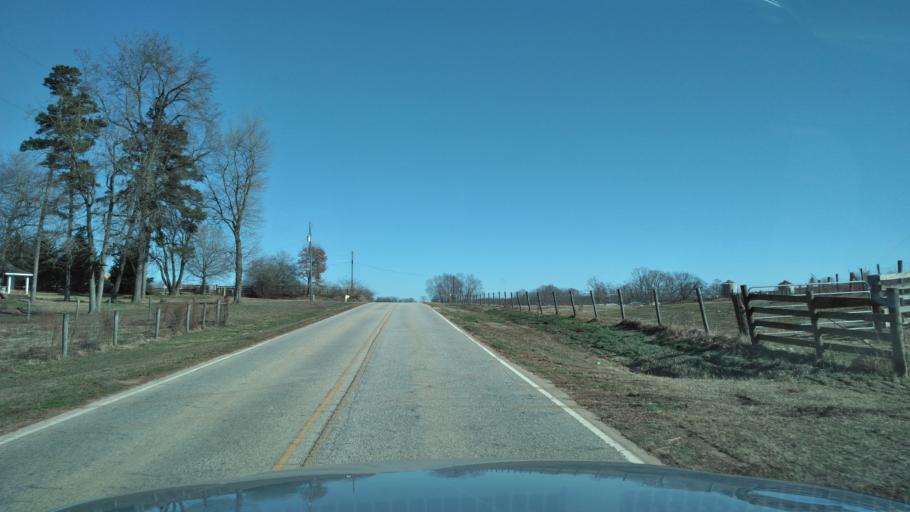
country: US
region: Georgia
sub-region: Hall County
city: Lula
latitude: 34.3194
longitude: -83.7073
